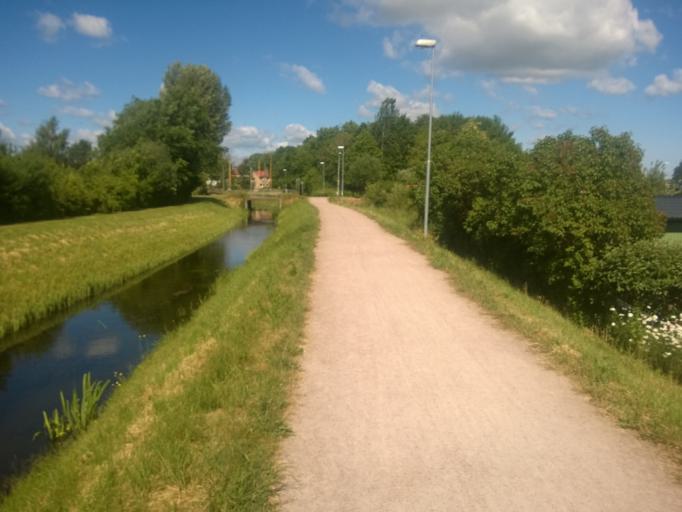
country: SE
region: Skane
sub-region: Kristianstads Kommun
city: Kristianstad
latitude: 56.0499
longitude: 14.1878
